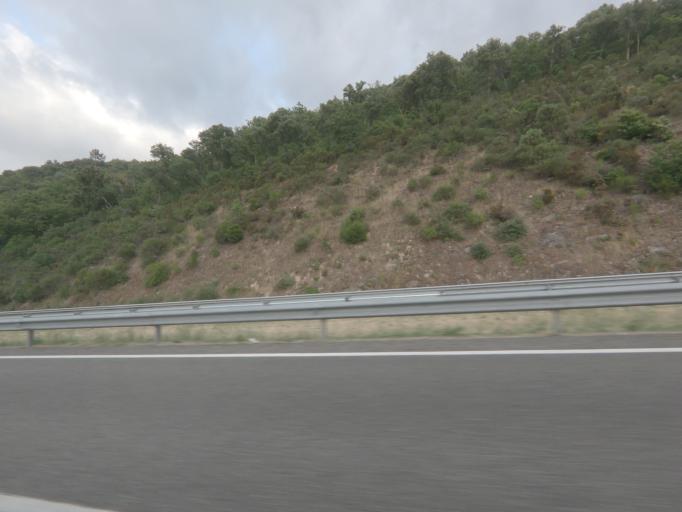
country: ES
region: Galicia
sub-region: Provincia de Ourense
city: Toen
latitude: 42.3342
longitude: -7.9452
